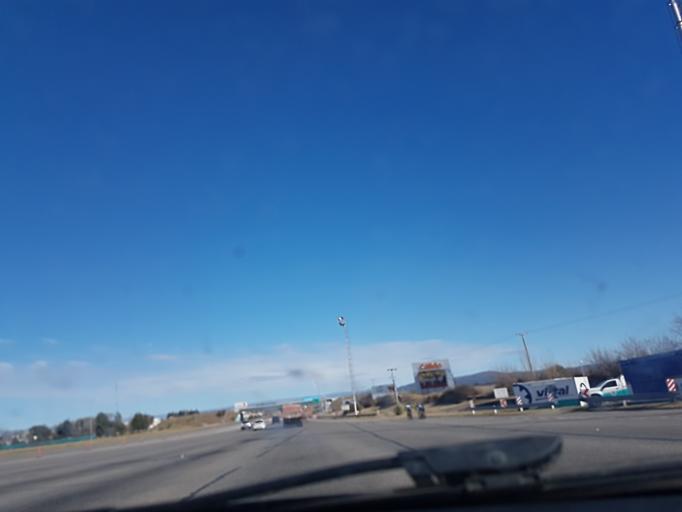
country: AR
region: Cordoba
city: Malagueno
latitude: -31.4364
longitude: -64.3126
